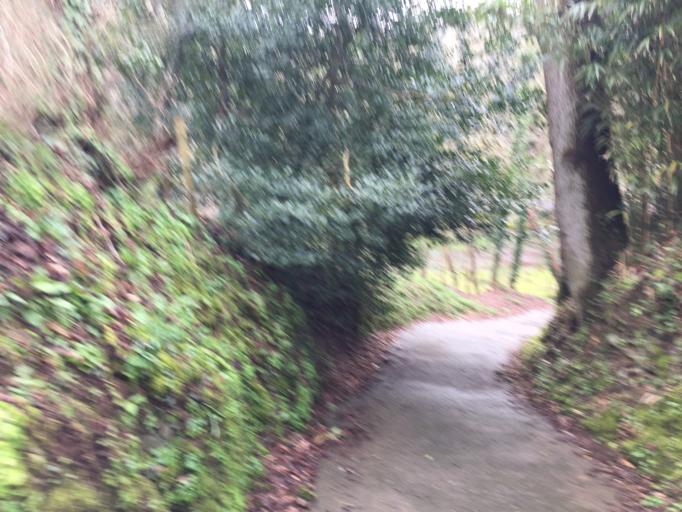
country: JE
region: St Helier
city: Saint Helier
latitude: 49.2145
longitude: -2.1336
